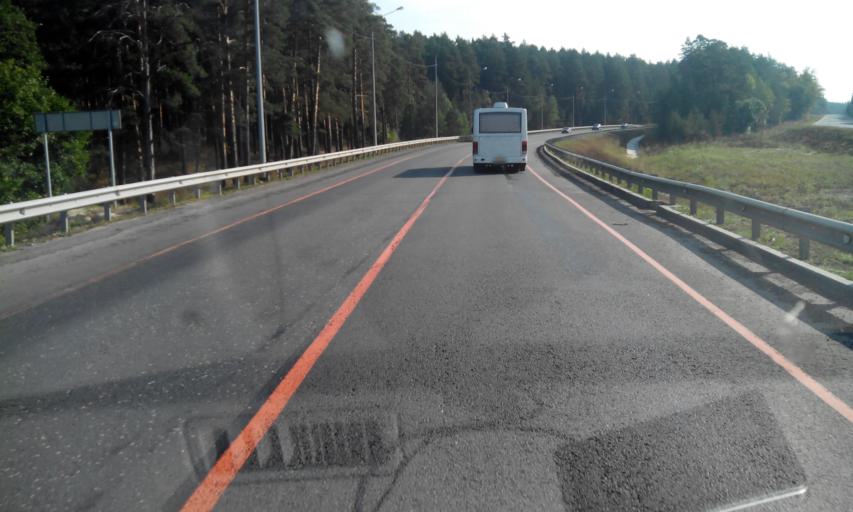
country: RU
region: Penza
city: Srednyaya Yelyuzan'
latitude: 53.0855
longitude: 46.0544
